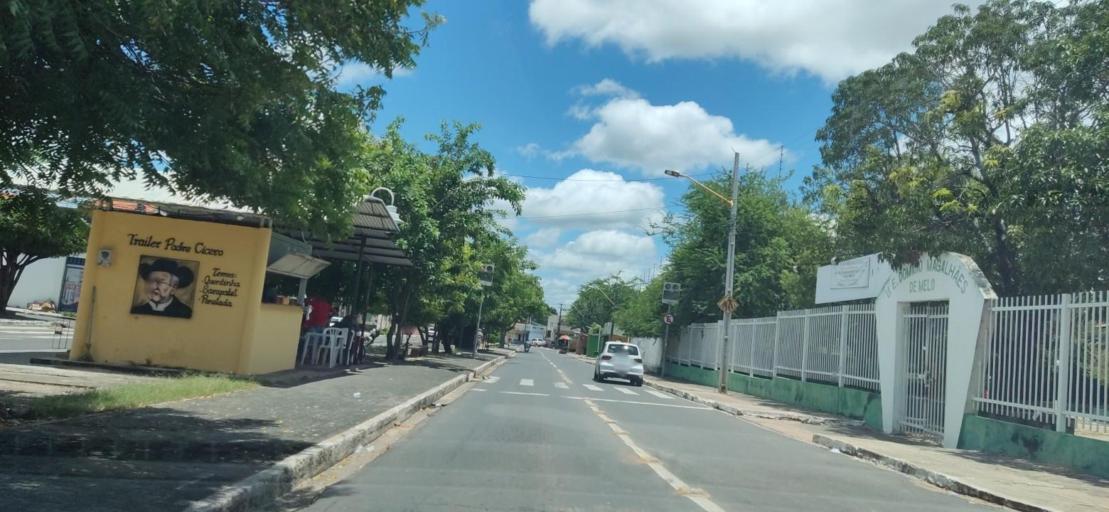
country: BR
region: Piaui
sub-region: Teresina
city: Teresina
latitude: -5.1498
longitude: -42.7842
